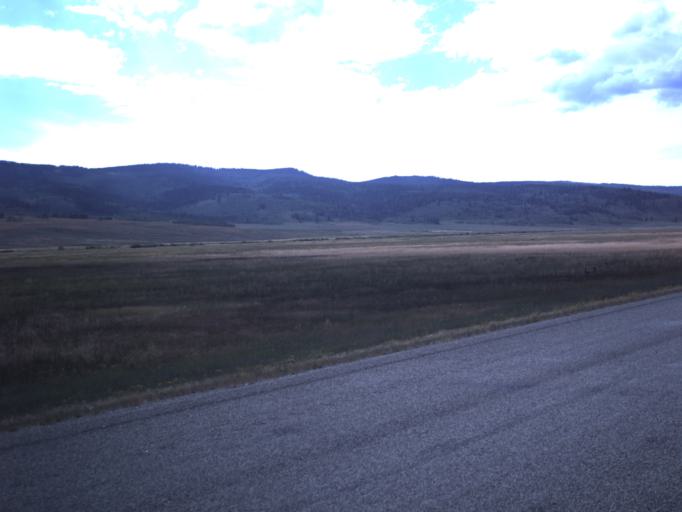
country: US
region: Utah
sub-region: Wasatch County
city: Heber
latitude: 40.2524
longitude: -111.1962
